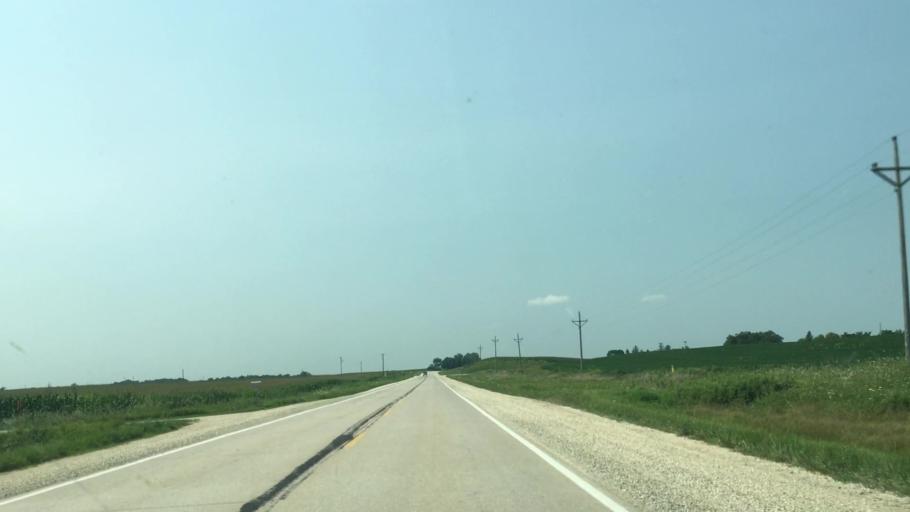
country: US
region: Iowa
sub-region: Fayette County
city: West Union
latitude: 43.0946
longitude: -91.8599
